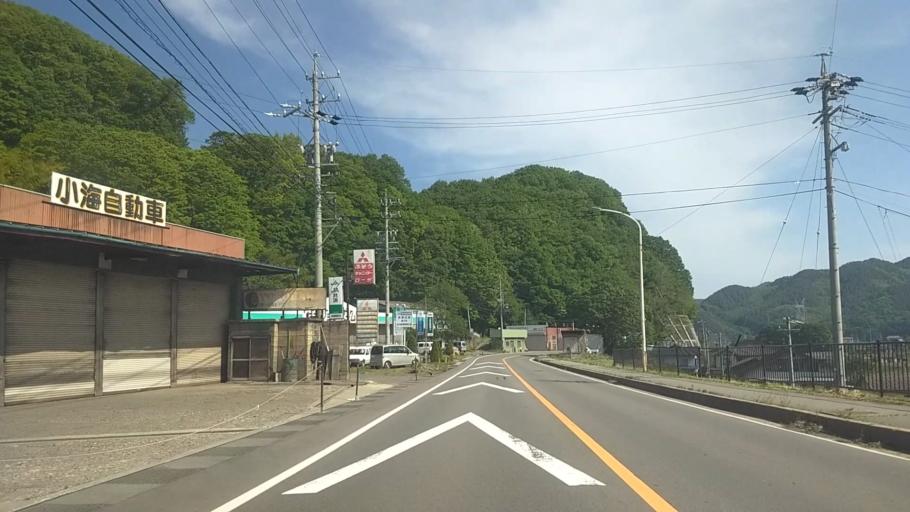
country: JP
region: Nagano
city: Saku
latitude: 36.0964
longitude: 138.4827
